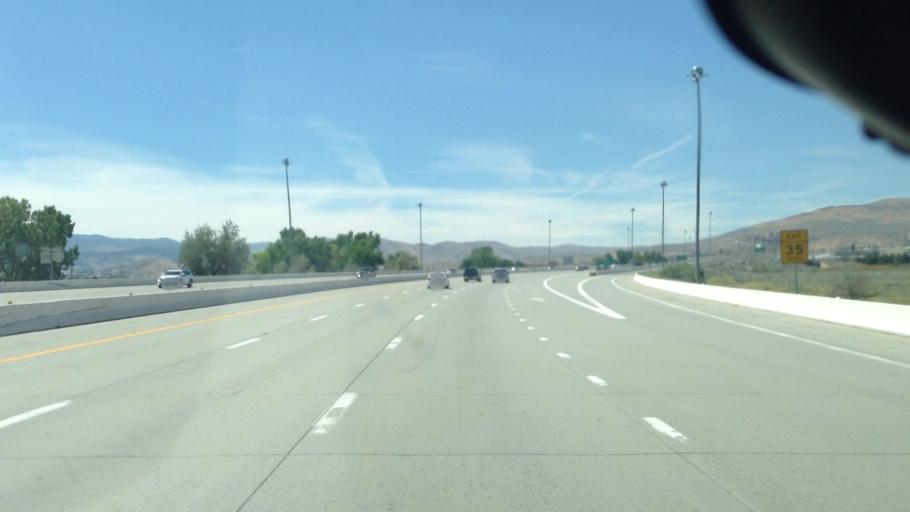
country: US
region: Nevada
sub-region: Washoe County
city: Sparks
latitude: 39.4160
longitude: -119.7471
